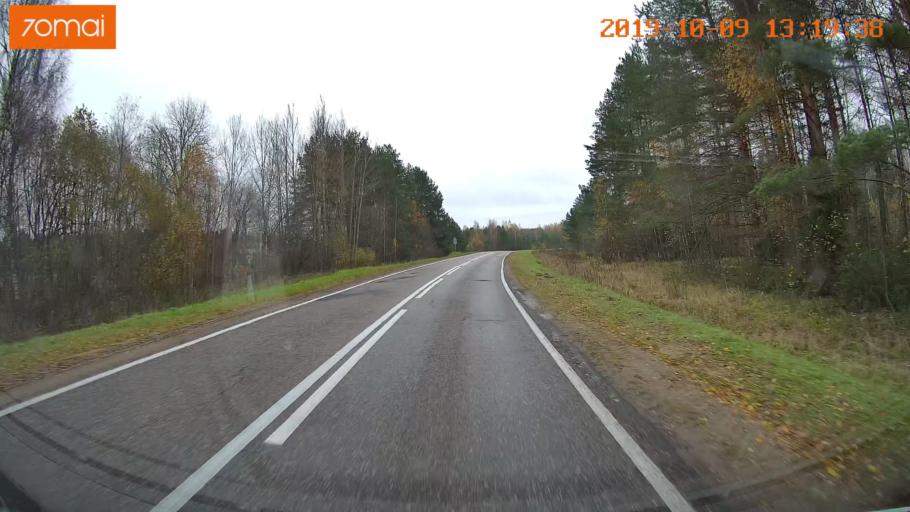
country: RU
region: Jaroslavl
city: Lyubim
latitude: 58.3488
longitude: 40.8173
